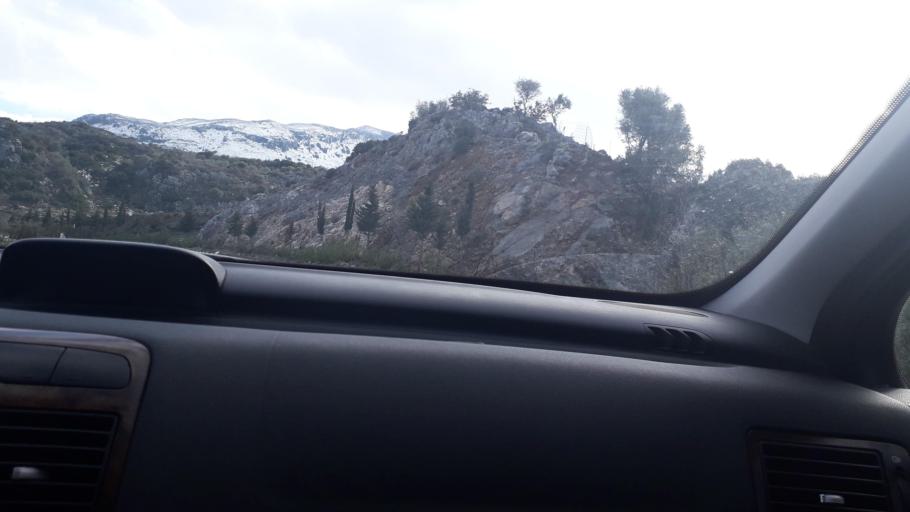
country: GR
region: Crete
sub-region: Nomos Rethymnis
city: Agia Foteini
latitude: 35.2626
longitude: 24.5614
